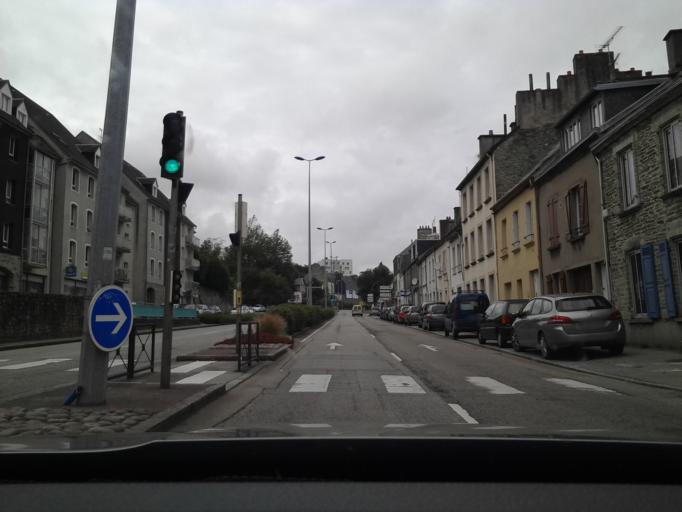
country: FR
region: Lower Normandy
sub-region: Departement de la Manche
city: Cherbourg-Octeville
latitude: 49.6352
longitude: -1.6287
